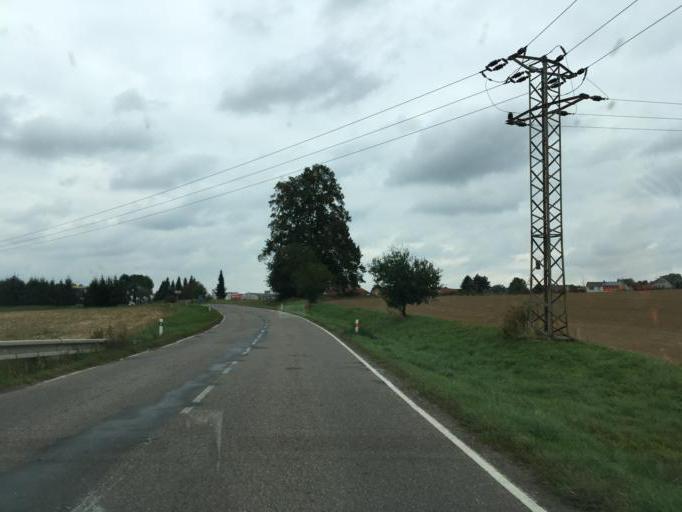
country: CZ
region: Central Bohemia
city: Cechtice
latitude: 49.6273
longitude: 15.0415
